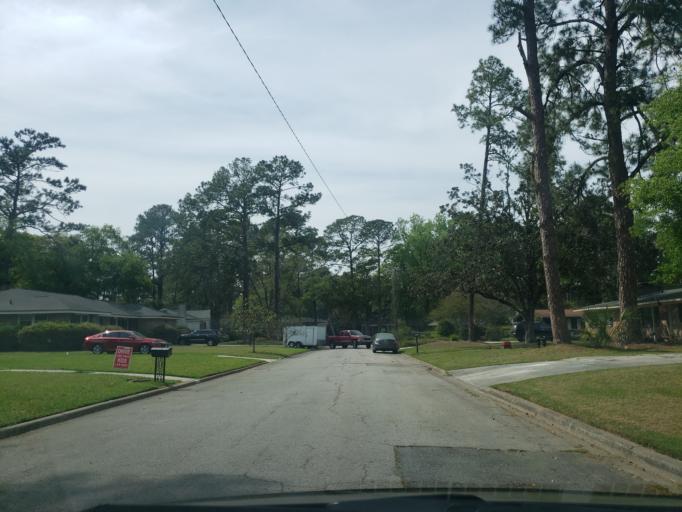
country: US
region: Georgia
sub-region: Chatham County
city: Isle of Hope
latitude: 31.9952
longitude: -81.0974
